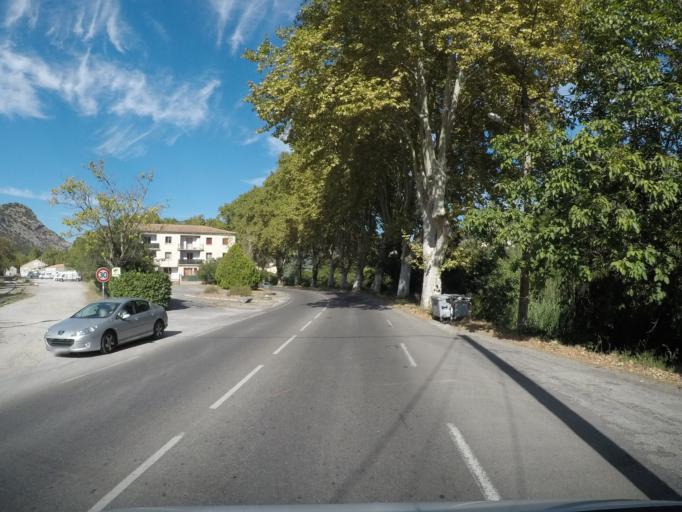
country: FR
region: Languedoc-Roussillon
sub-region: Departement du Gard
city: Anduze
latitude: 44.0470
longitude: 3.9854
